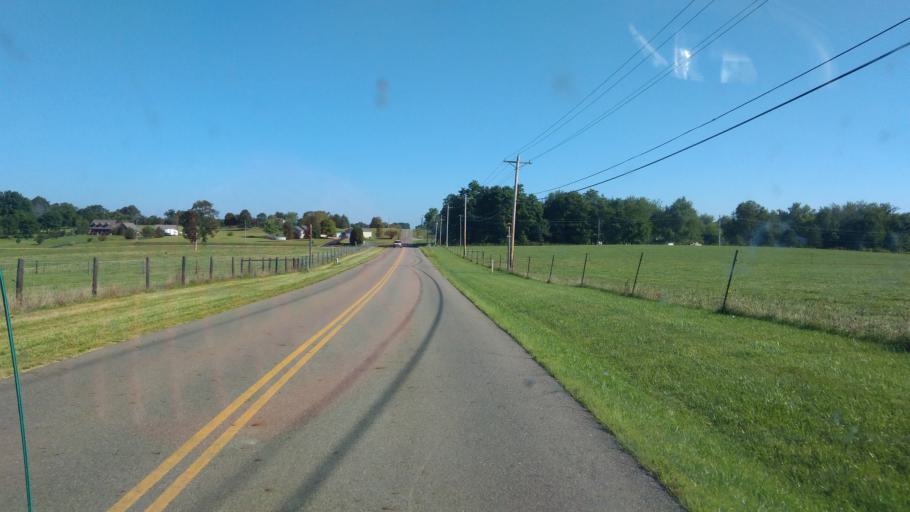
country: US
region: Ohio
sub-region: Knox County
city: Gambier
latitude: 40.4295
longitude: -82.3675
